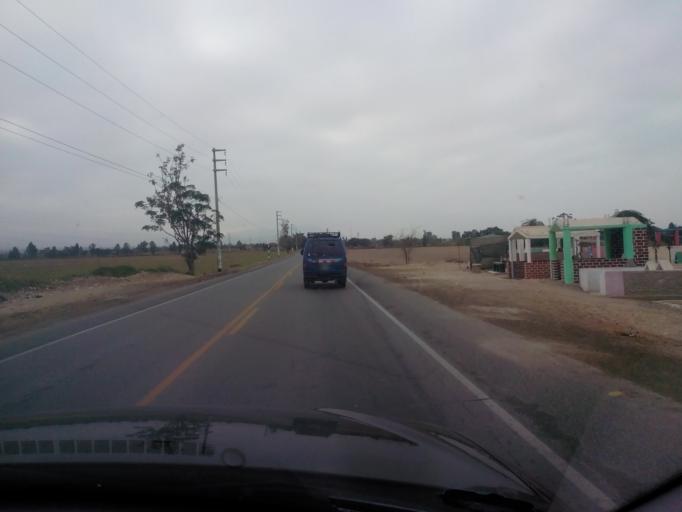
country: PE
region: Ica
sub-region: Provincia de Pisco
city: Independencia
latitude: -13.6859
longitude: -76.0450
